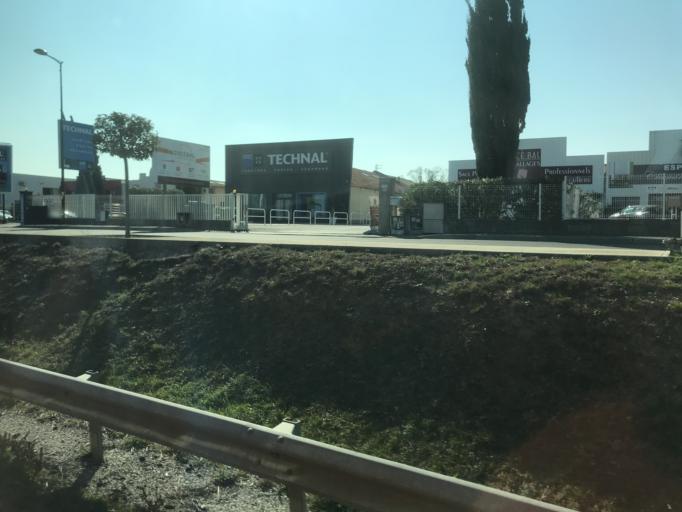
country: FR
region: Languedoc-Roussillon
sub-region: Departement de l'Herault
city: Perols
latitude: 43.5829
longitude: 3.9424
